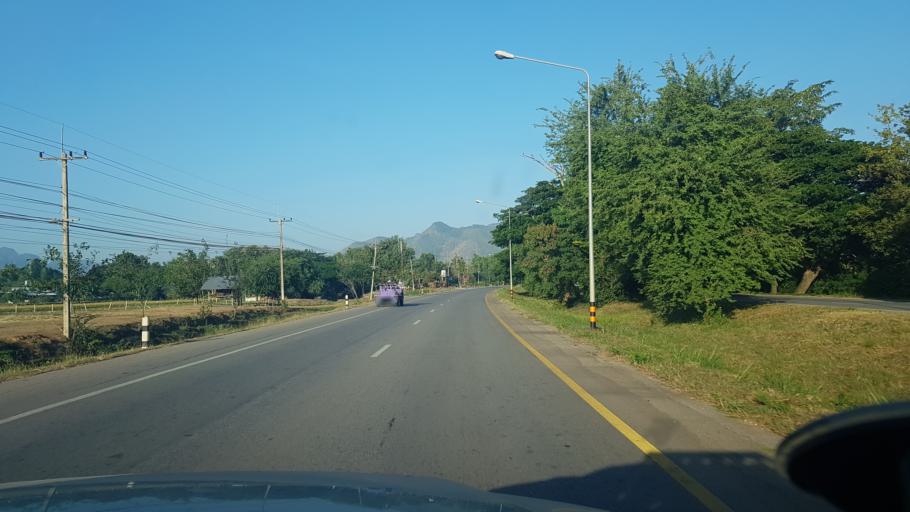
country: TH
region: Chaiyaphum
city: Khon San
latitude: 16.5962
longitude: 101.9153
